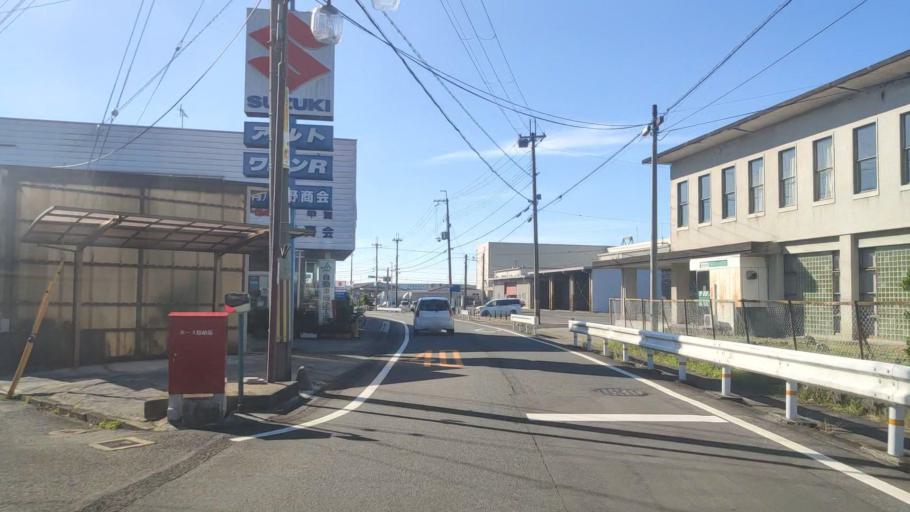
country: JP
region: Shiga Prefecture
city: Minakuchicho-matoba
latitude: 34.8904
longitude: 136.2295
